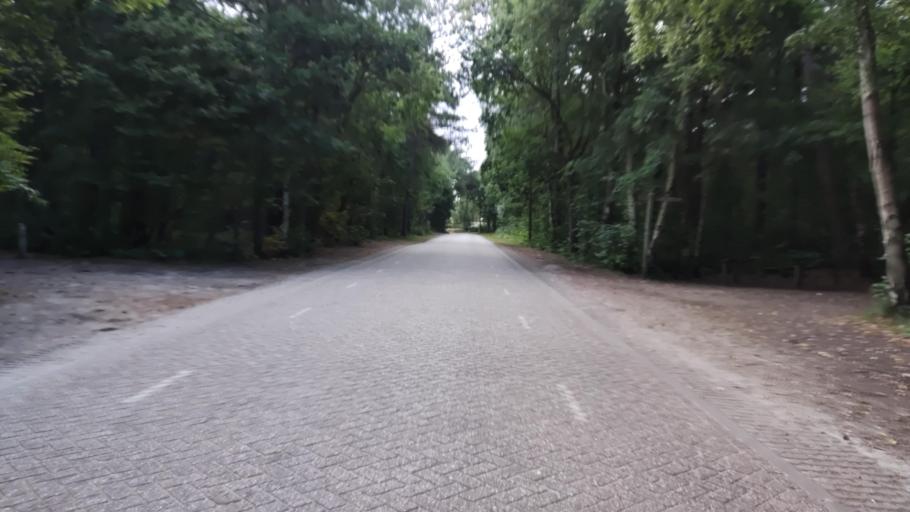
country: NL
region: North Holland
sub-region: Gemeente Texel
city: Den Burg
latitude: 53.0824
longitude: 4.7569
